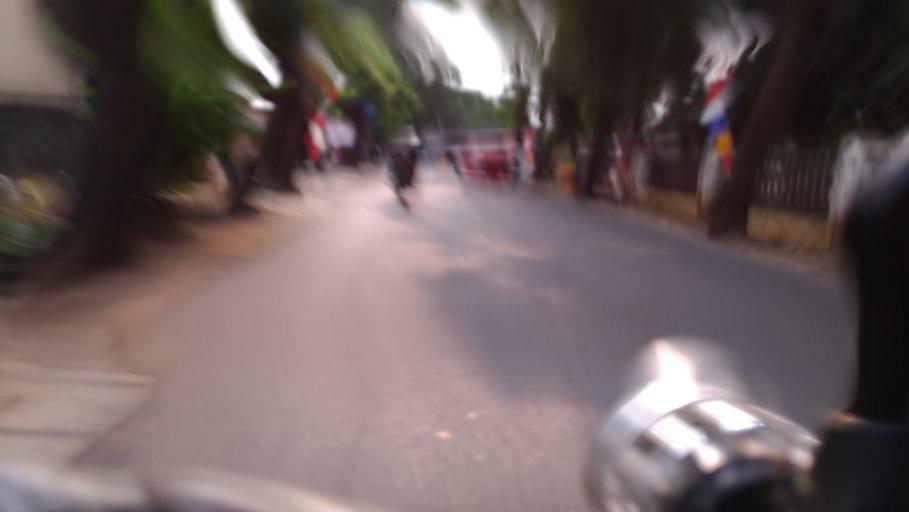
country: ID
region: West Java
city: Cileungsir
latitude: -6.3495
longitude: 106.8942
